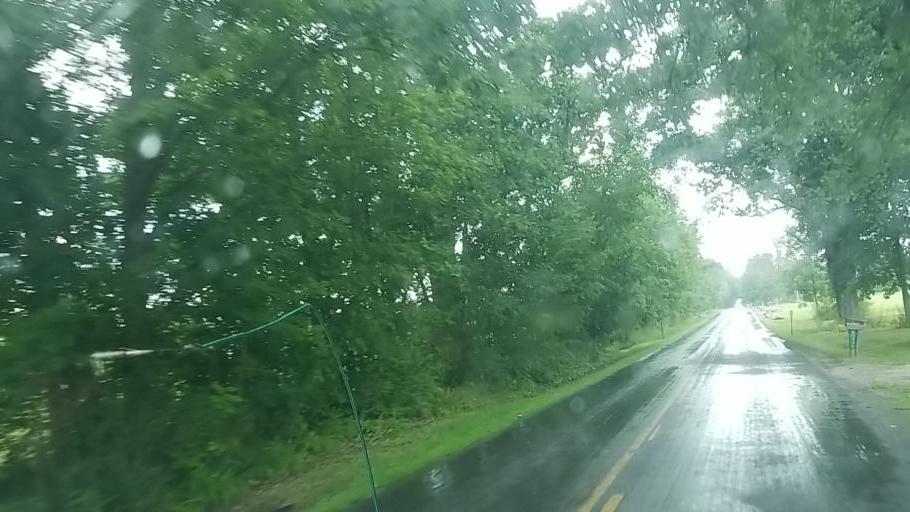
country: US
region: Ohio
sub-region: Lorain County
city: Lagrange
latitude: 41.1780
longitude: -82.0534
